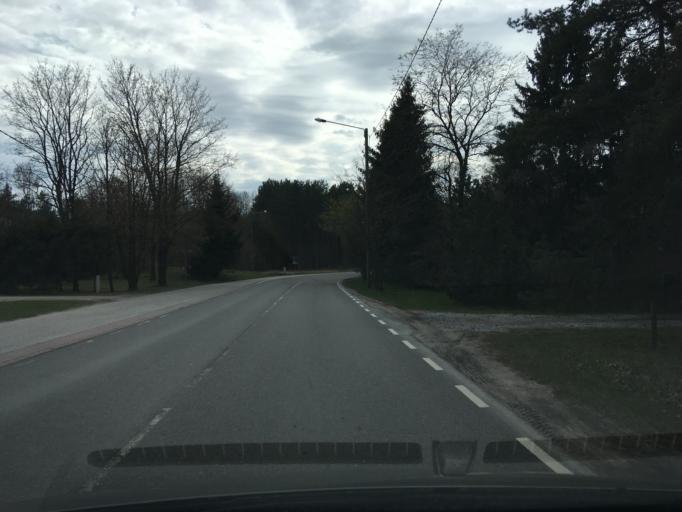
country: EE
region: Harju
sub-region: Tallinna linn
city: Kose
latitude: 59.4688
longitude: 24.9082
